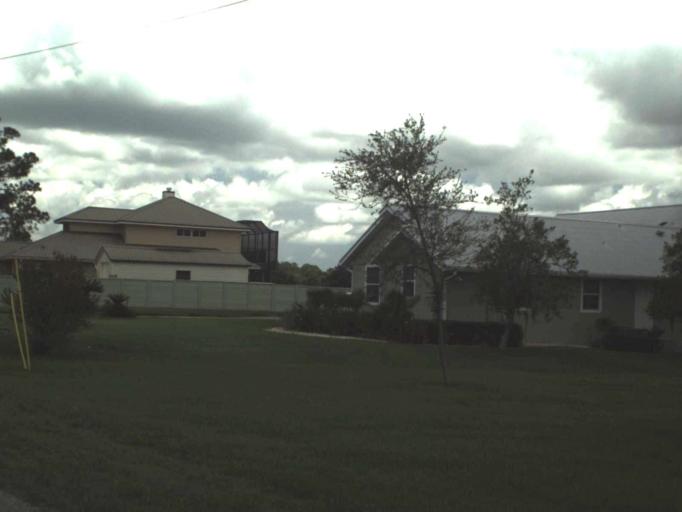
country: US
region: Florida
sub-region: Volusia County
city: Lake Helen
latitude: 29.0224
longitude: -81.2527
